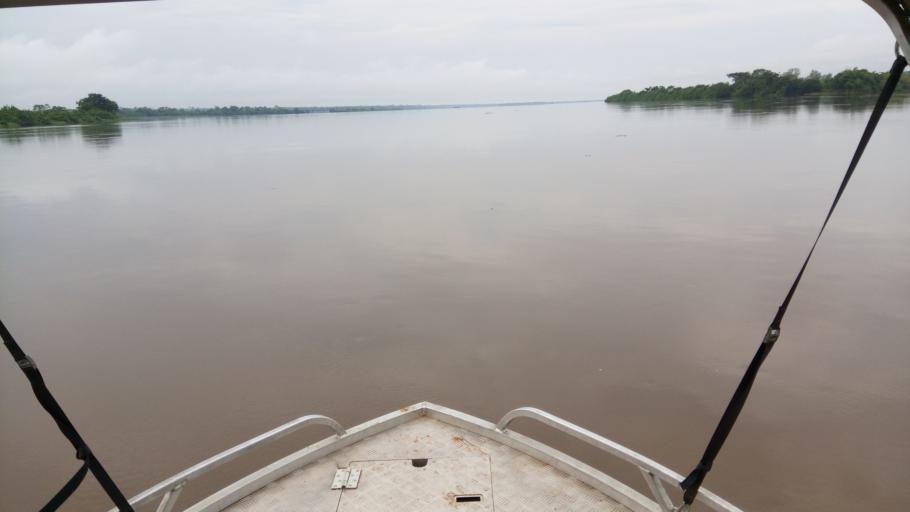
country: CD
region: Eastern Province
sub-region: Sous-Region de la Tshopo
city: Yangambi
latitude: 0.7540
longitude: 24.4291
